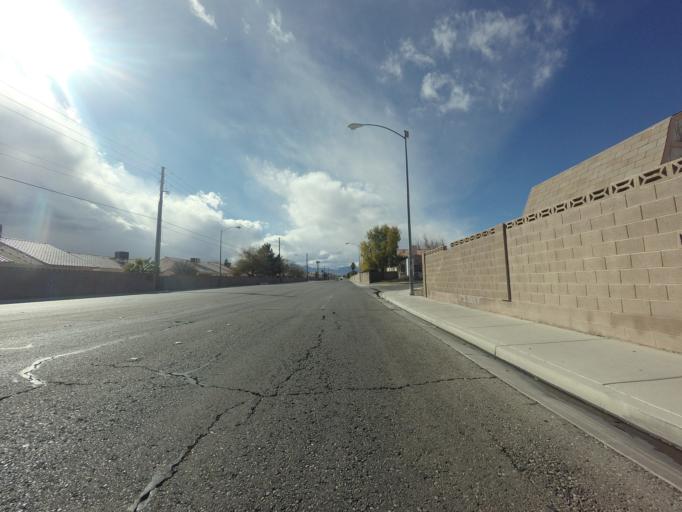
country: US
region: Nevada
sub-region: Clark County
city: North Las Vegas
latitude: 36.2544
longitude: -115.1478
